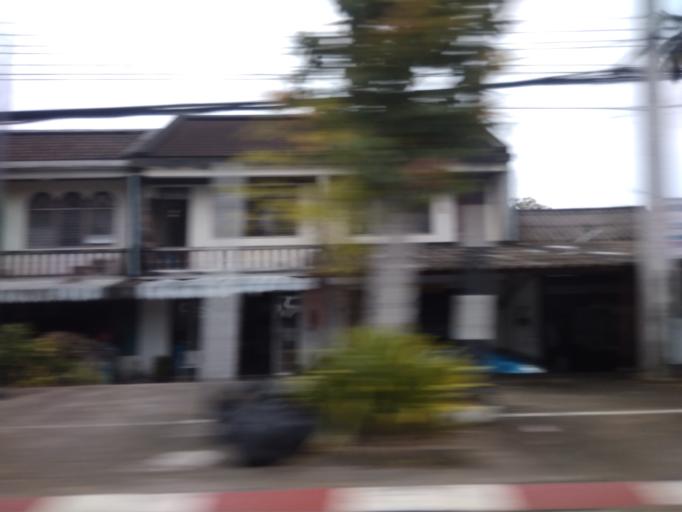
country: TH
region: Phuket
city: Mueang Phuket
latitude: 7.8592
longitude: 98.3805
